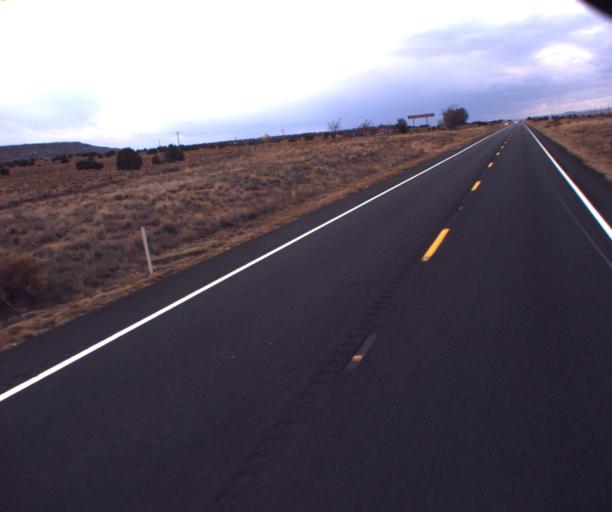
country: US
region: Arizona
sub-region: Coconino County
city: Kaibito
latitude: 36.4142
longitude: -110.8184
